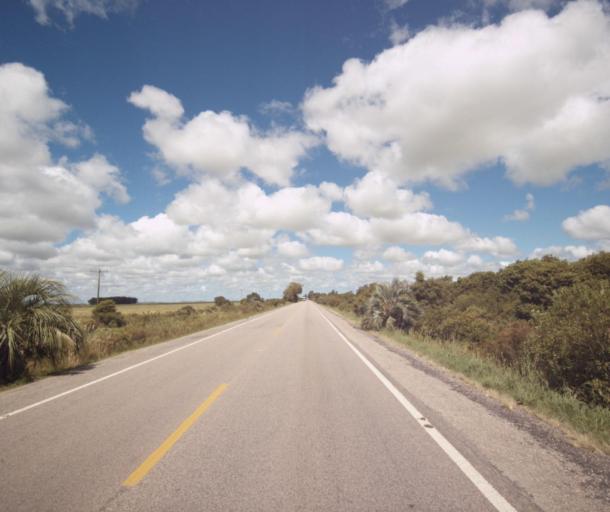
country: BR
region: Rio Grande do Sul
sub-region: Rio Grande
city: Rio Grande
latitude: -32.1789
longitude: -52.4213
